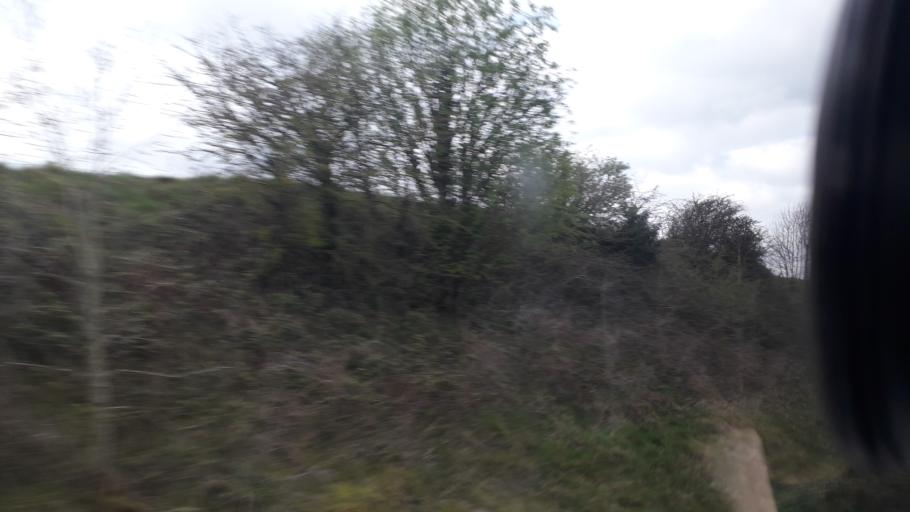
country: IE
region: Leinster
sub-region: An Iarmhi
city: An Muileann gCearr
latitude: 53.5632
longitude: -7.3631
